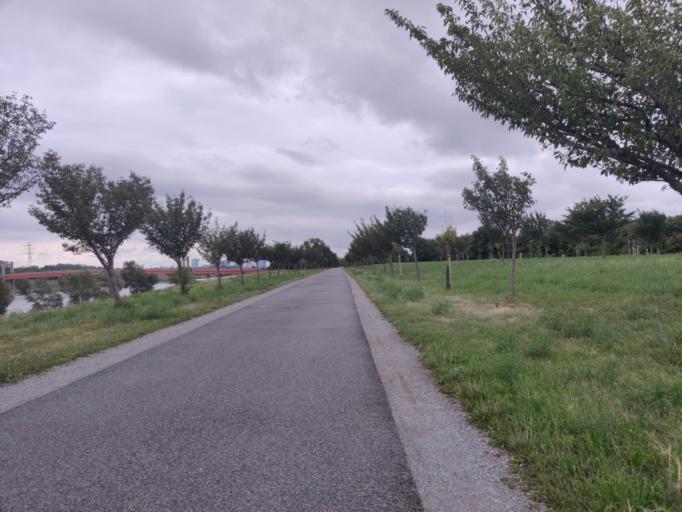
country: AT
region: Lower Austria
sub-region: Politischer Bezirk Korneuburg
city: Langenzersdorf
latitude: 48.2701
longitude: 16.3691
